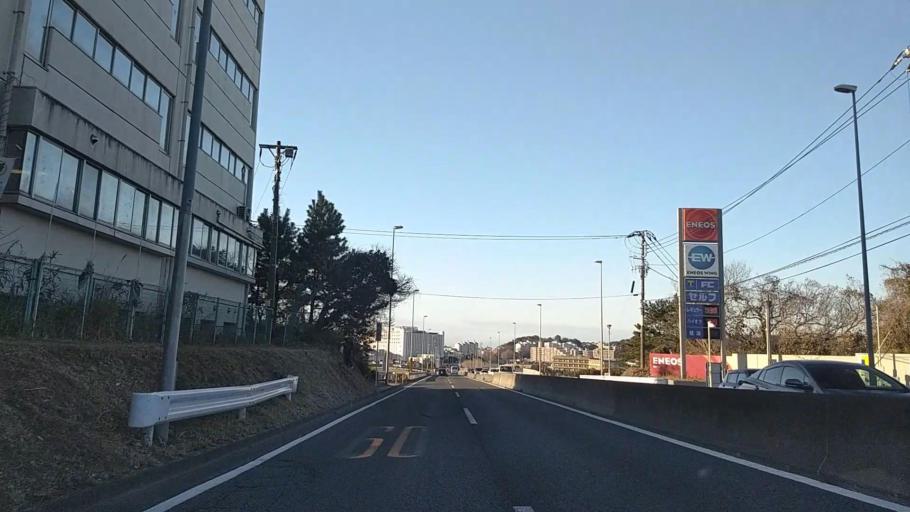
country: JP
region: Kanagawa
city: Fujisawa
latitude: 35.3563
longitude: 139.4889
